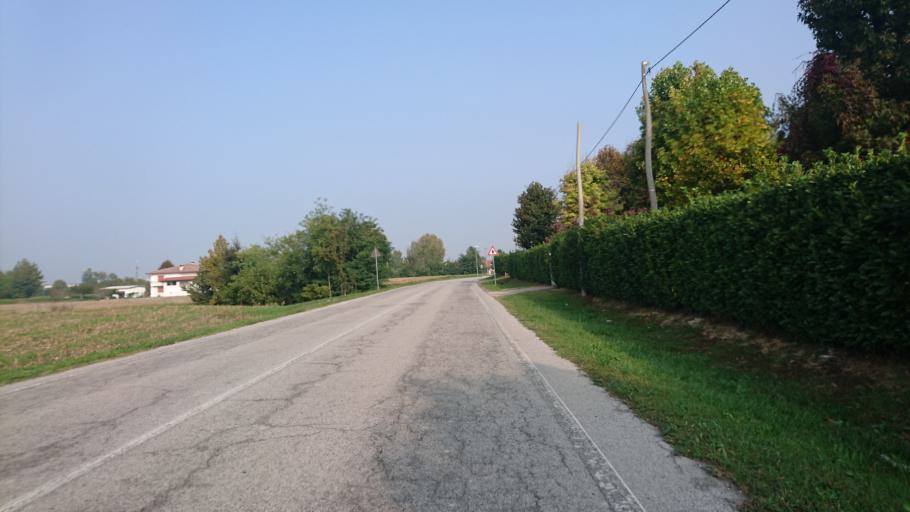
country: IT
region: Veneto
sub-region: Provincia di Padova
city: Curtarolo
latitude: 45.5274
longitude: 11.8425
